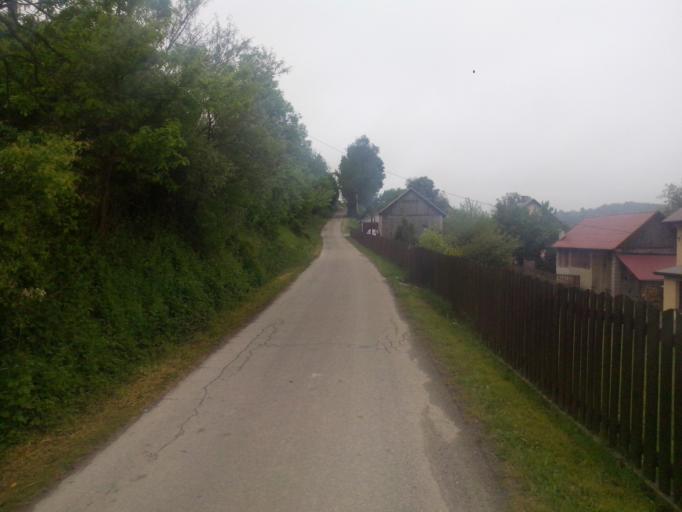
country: PL
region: Subcarpathian Voivodeship
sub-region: Powiat strzyzowski
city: Strzyzow
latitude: 49.8686
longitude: 21.8104
